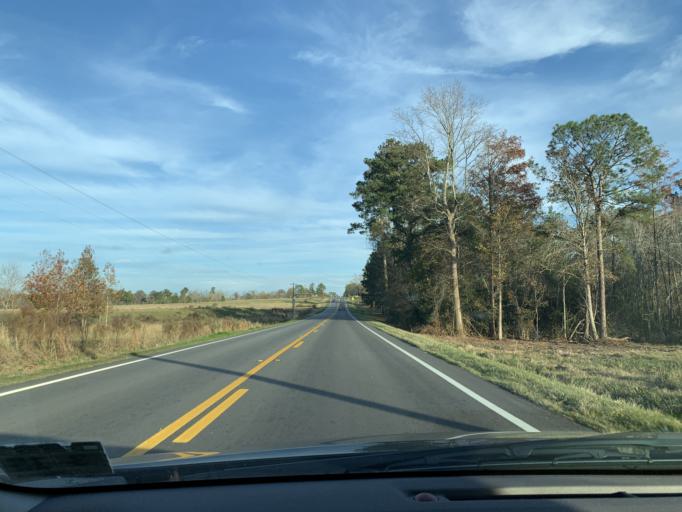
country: US
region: Georgia
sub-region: Irwin County
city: Ocilla
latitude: 31.5959
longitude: -83.1631
